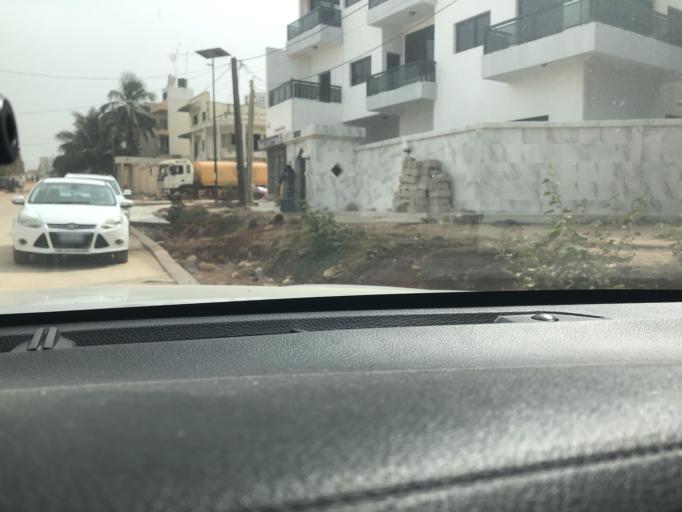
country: SN
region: Dakar
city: Mermoz Boabab
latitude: 14.7293
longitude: -17.4975
